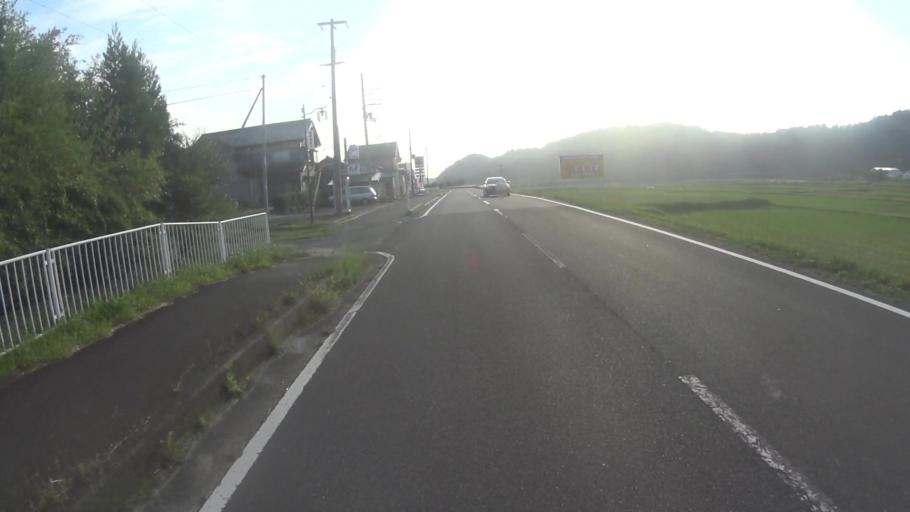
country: JP
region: Kyoto
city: Miyazu
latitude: 35.6498
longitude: 135.0915
